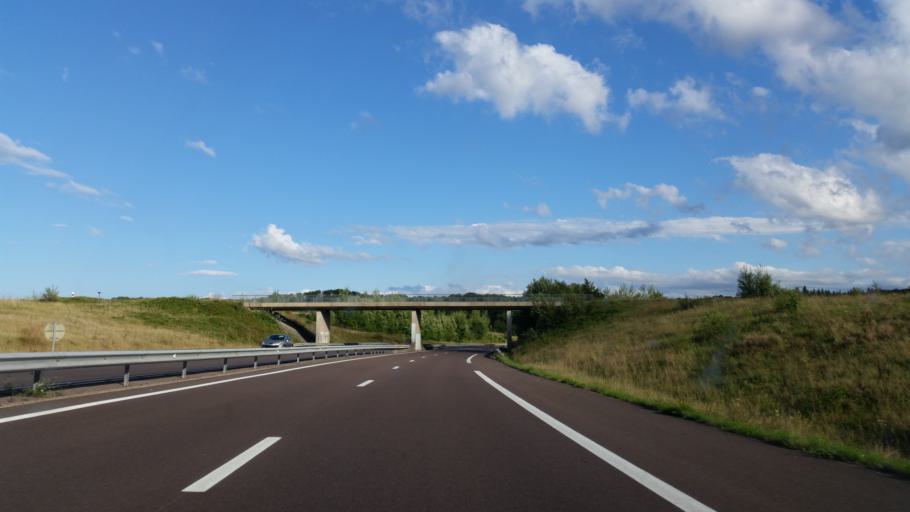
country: FR
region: Franche-Comte
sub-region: Departement de la Haute-Saone
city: Roye
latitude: 47.6506
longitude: 6.5870
